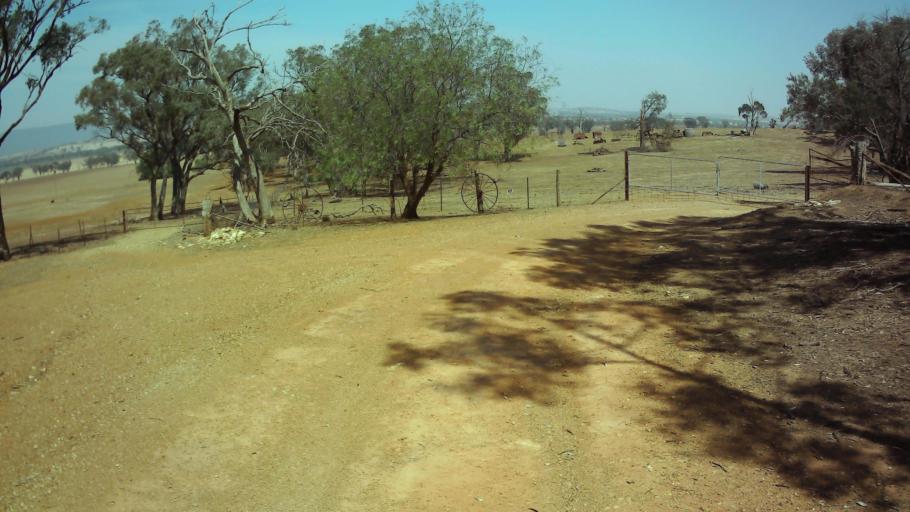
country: AU
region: New South Wales
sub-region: Weddin
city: Grenfell
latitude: -33.8931
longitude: 148.1120
